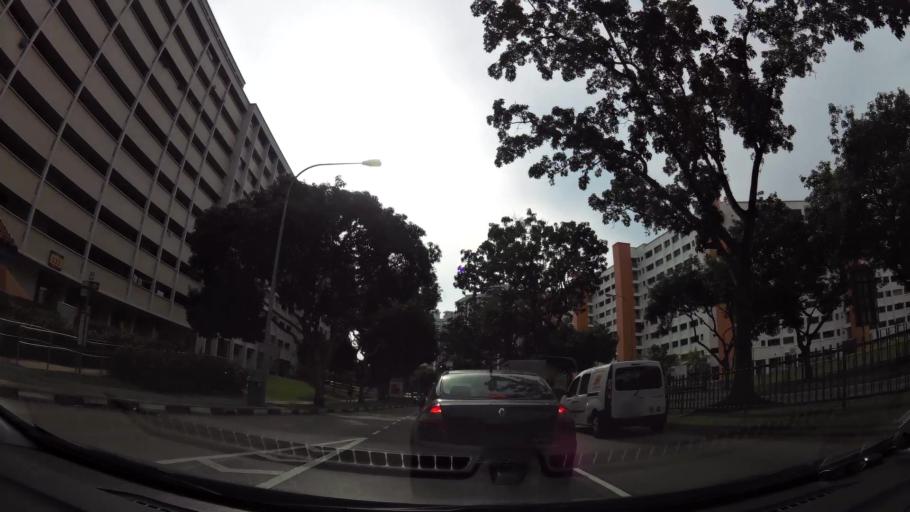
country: SG
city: Singapore
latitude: 1.3764
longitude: 103.8914
